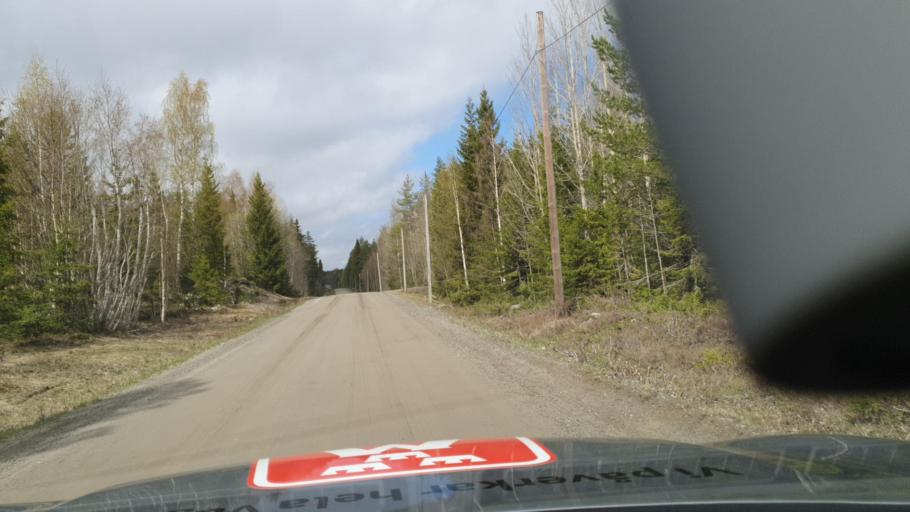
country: SE
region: Vaesterbotten
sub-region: Bjurholms Kommun
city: Bjurholm
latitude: 63.6748
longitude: 18.9947
